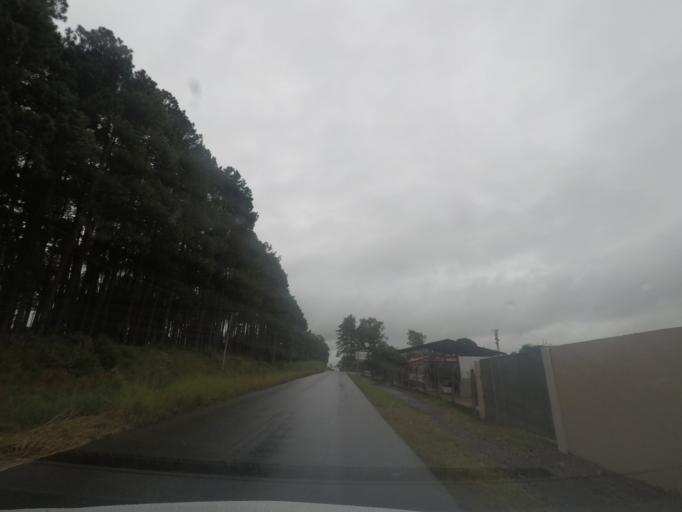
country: BR
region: Parana
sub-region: Quatro Barras
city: Quatro Barras
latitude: -25.3844
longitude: -49.1357
